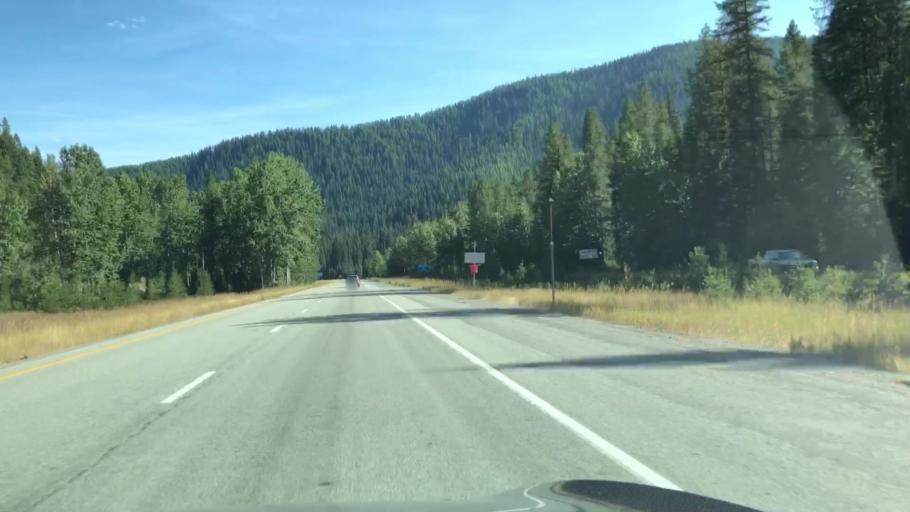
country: US
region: Idaho
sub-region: Shoshone County
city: Wallace
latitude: 47.4283
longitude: -115.6402
